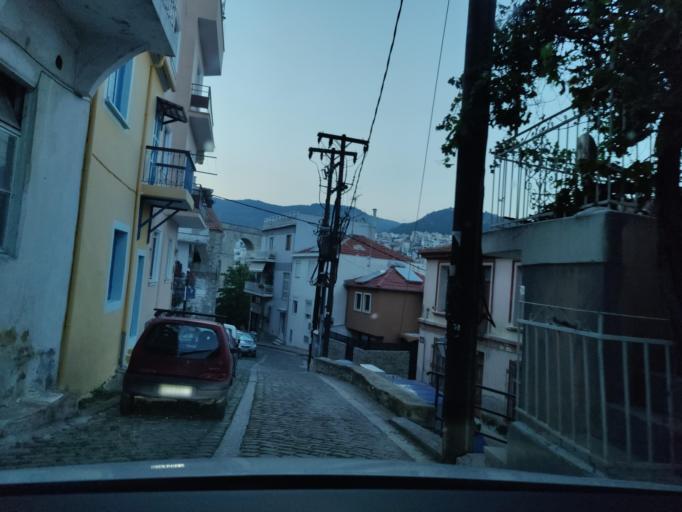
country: GR
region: East Macedonia and Thrace
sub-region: Nomos Kavalas
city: Kavala
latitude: 40.9359
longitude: 24.4163
